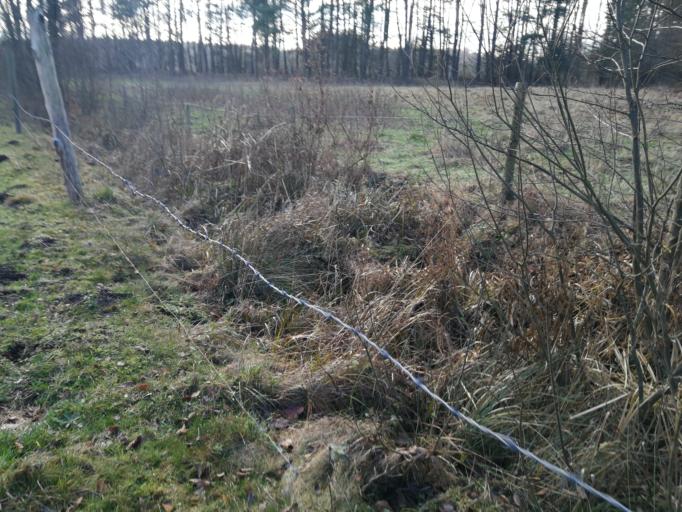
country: PL
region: Warmian-Masurian Voivodeship
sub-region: Powiat dzialdowski
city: Rybno
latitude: 53.4134
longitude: 19.9079
